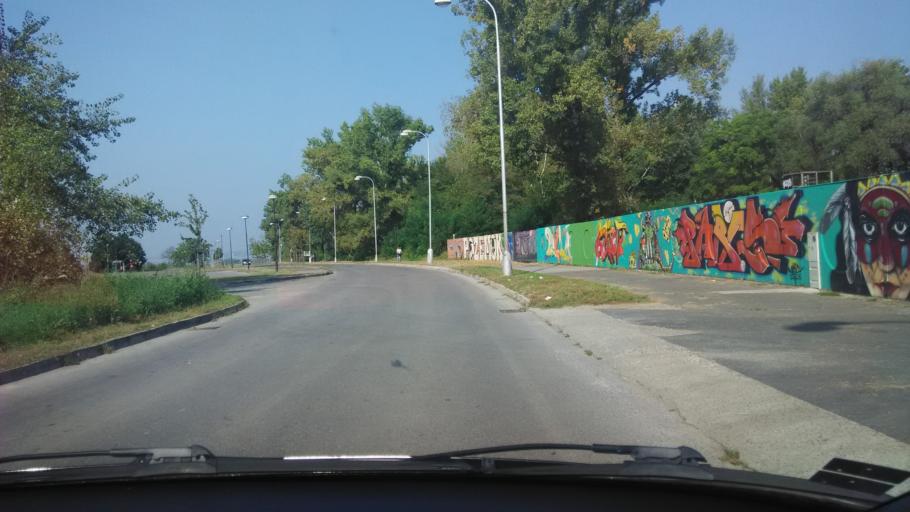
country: SK
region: Trnavsky
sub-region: Okres Trnava
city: Piestany
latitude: 48.5747
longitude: 17.8165
